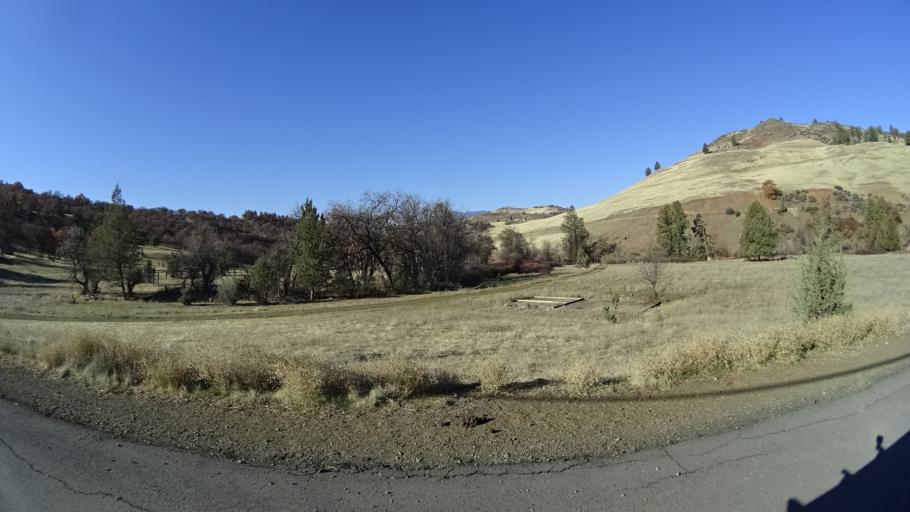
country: US
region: California
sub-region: Siskiyou County
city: Montague
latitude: 41.9183
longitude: -122.4487
